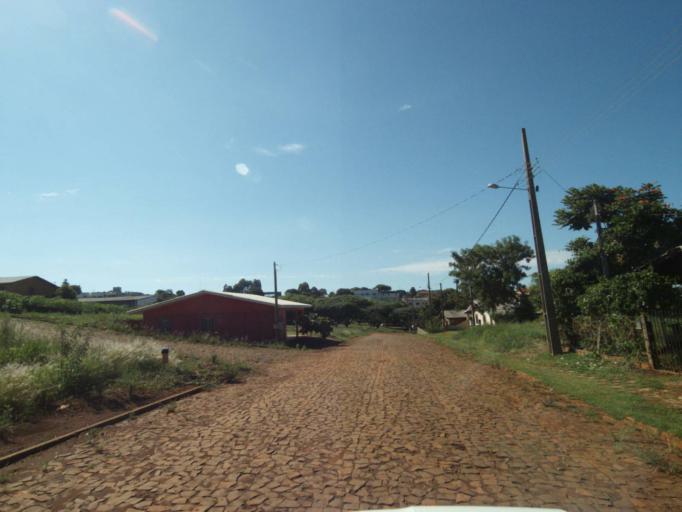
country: BR
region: Parana
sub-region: Laranjeiras Do Sul
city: Laranjeiras do Sul
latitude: -25.4870
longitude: -52.5267
